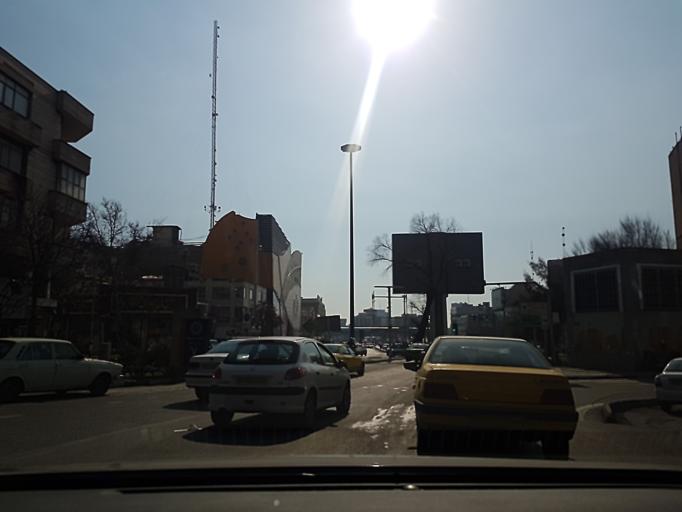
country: IR
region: Tehran
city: Tehran
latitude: 35.7196
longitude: 51.4282
